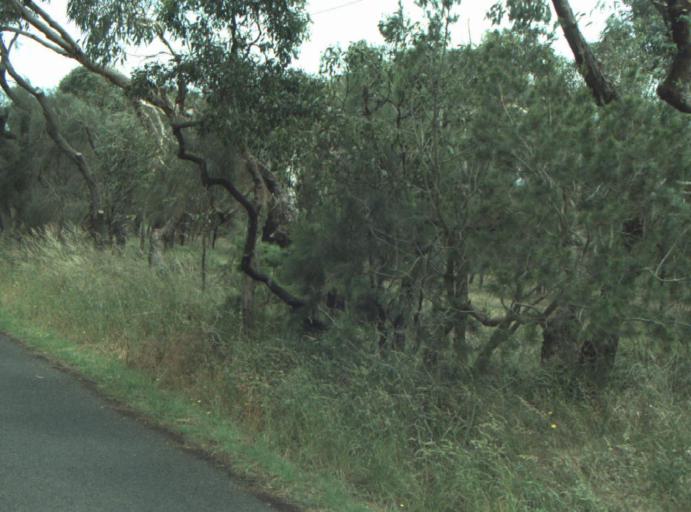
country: AU
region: Victoria
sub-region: Greater Geelong
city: Clifton Springs
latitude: -38.2156
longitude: 144.5626
